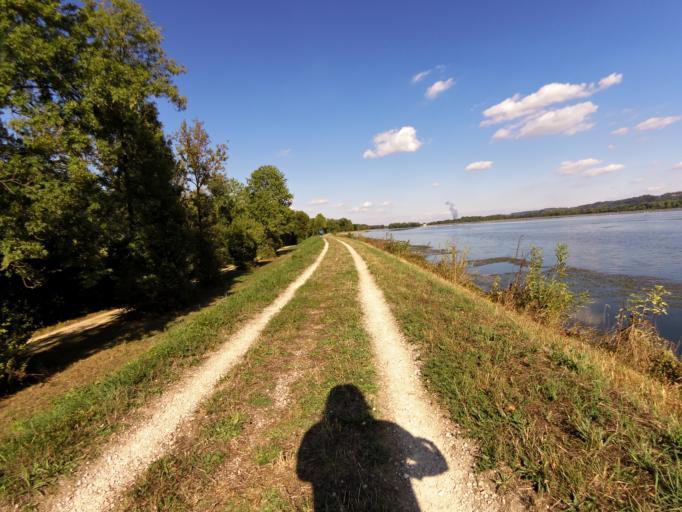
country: DE
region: Bavaria
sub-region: Lower Bavaria
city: Ergolding
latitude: 48.5741
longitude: 12.1993
